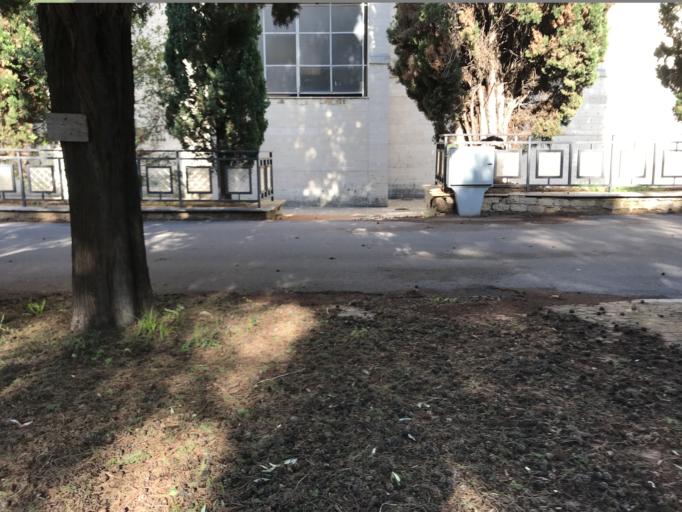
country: IT
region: Latium
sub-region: Citta metropolitana di Roma Capitale
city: Rome
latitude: 41.9022
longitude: 12.5301
